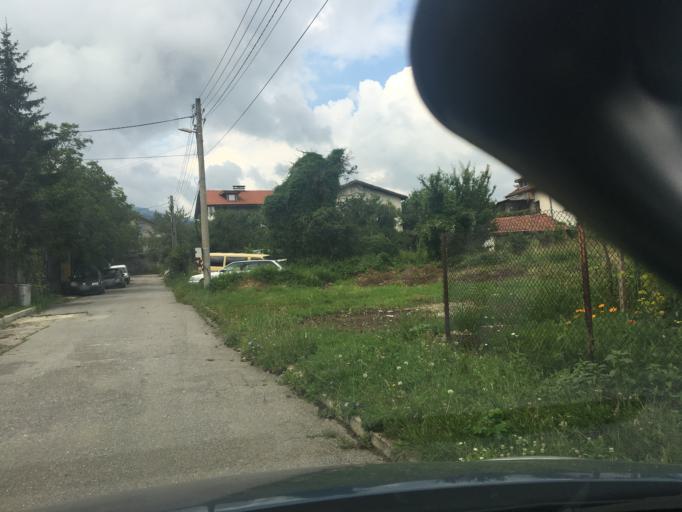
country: BG
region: Sofia-Capital
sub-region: Stolichna Obshtina
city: Sofia
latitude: 42.5855
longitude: 23.3692
